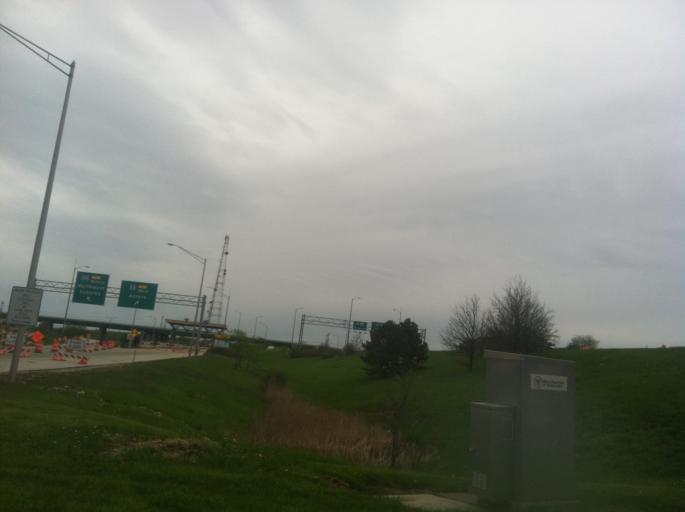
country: US
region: Illinois
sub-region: DuPage County
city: Lisle
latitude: 41.8040
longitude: -88.0541
